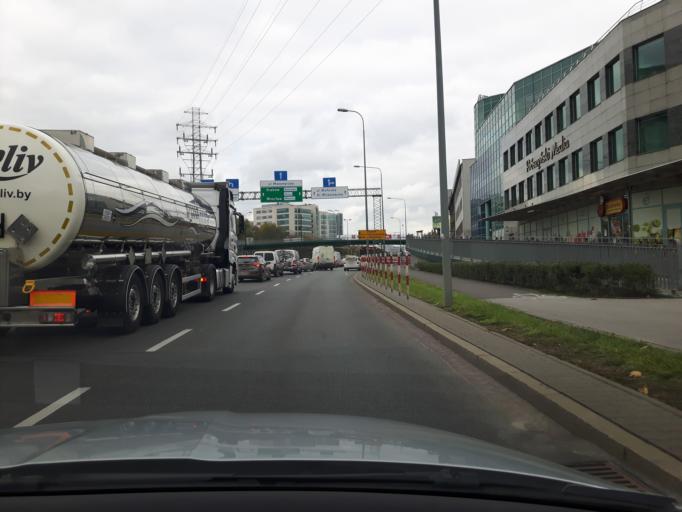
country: PL
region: Masovian Voivodeship
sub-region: Warszawa
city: Mokotow
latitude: 52.1739
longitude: 21.0028
